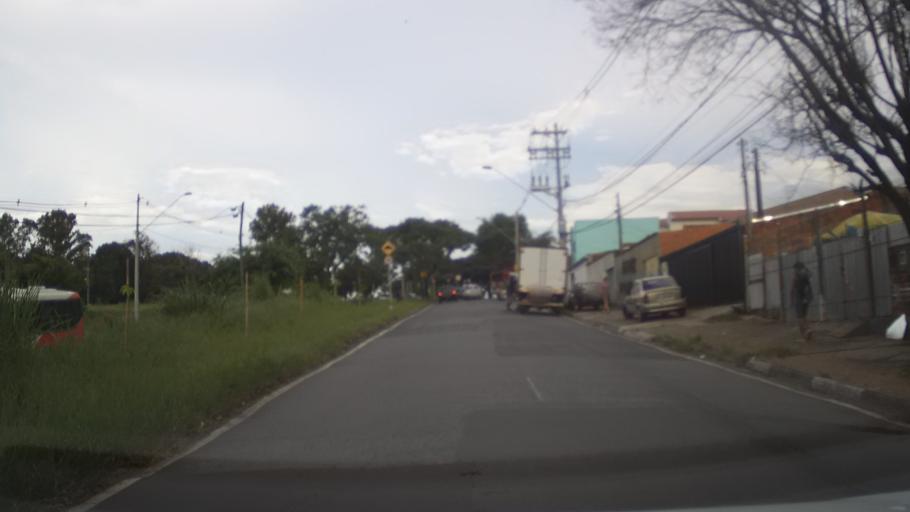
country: BR
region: Sao Paulo
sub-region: Hortolandia
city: Hortolandia
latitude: -22.9532
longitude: -47.1920
